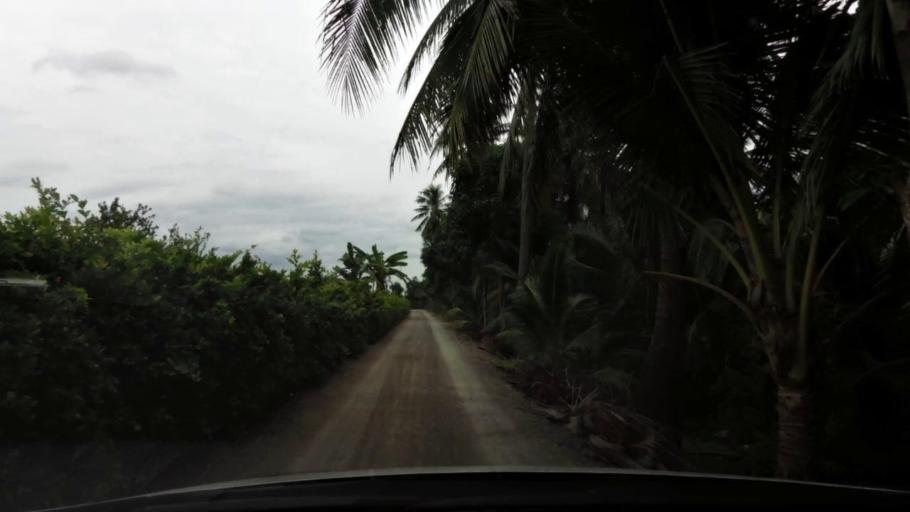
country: TH
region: Ratchaburi
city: Damnoen Saduak
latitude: 13.5619
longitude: 100.0071
